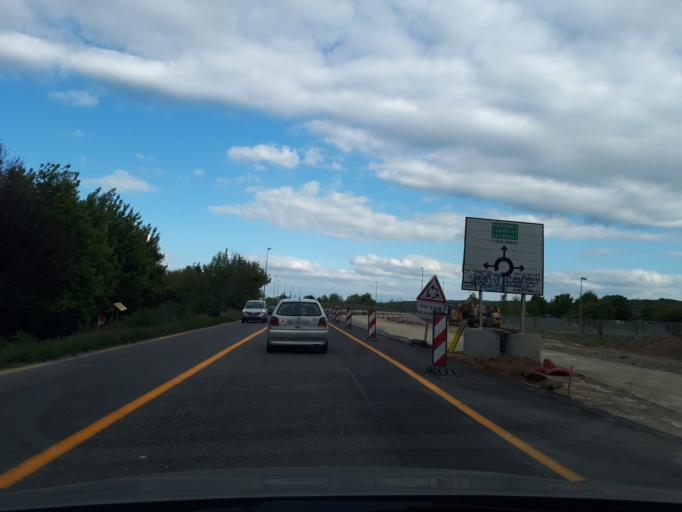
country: FR
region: Rhone-Alpes
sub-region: Departement de l'Isere
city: Vaulx-Milieu
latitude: 45.6229
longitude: 5.1745
